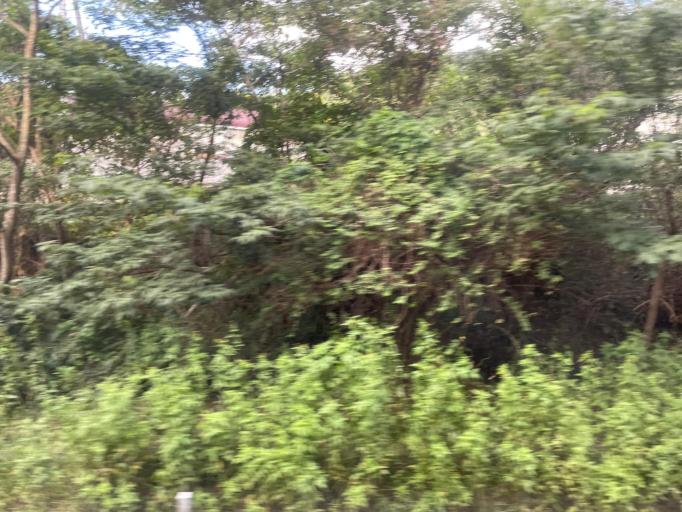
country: JP
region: Mie
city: Toba
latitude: 34.3899
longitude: 136.8113
